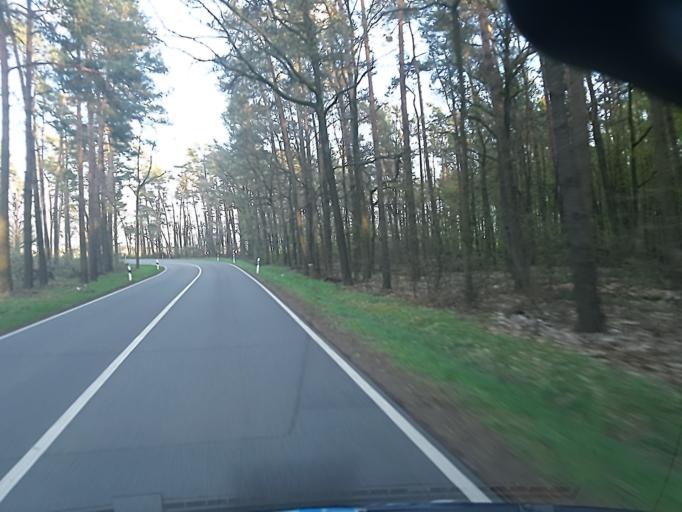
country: DE
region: Saxony
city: Trossin
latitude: 51.5656
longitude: 12.8282
